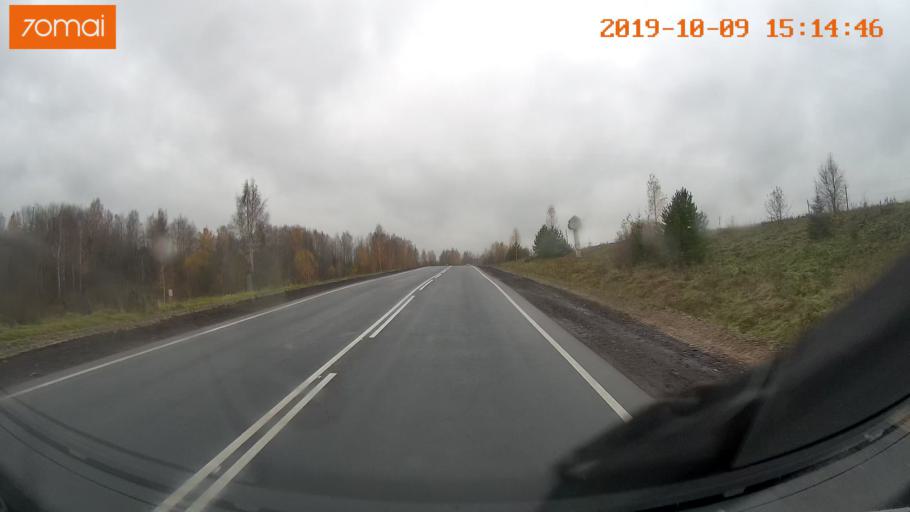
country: RU
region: Kostroma
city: Susanino
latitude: 58.1300
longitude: 41.6004
